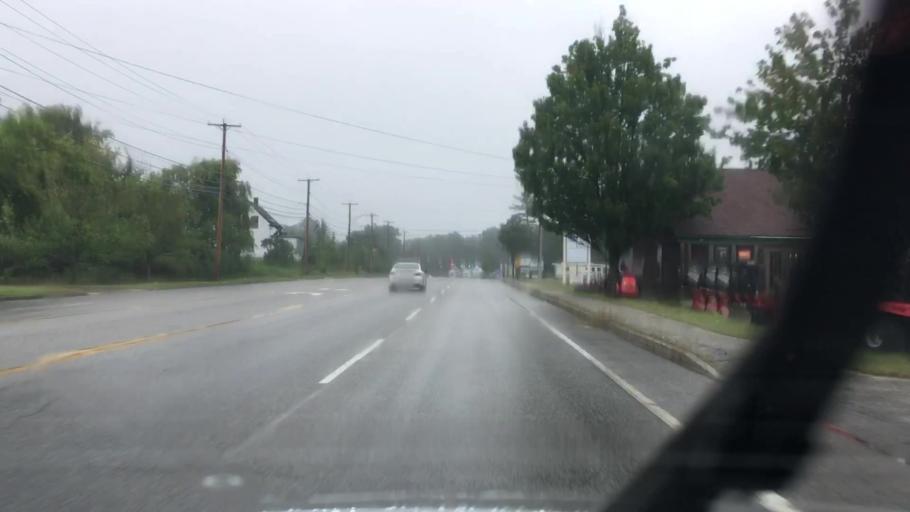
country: US
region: Maine
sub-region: Cumberland County
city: North Windham
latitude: 43.8457
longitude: -70.4472
